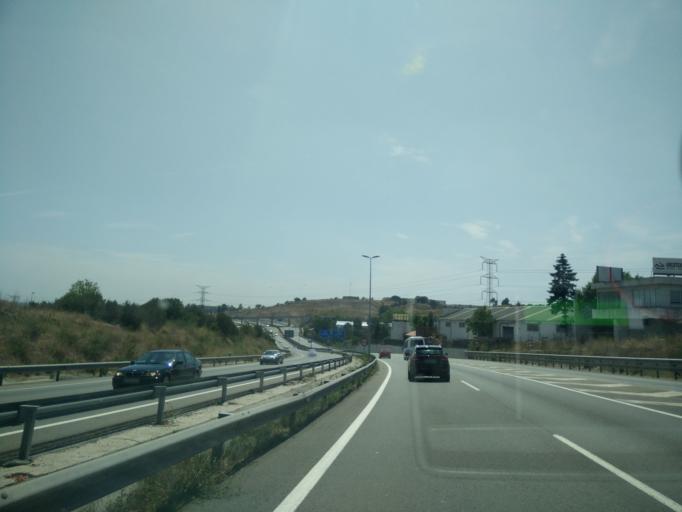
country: ES
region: Catalonia
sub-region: Provincia de Barcelona
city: Esparreguera
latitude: 41.5267
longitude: 1.8803
